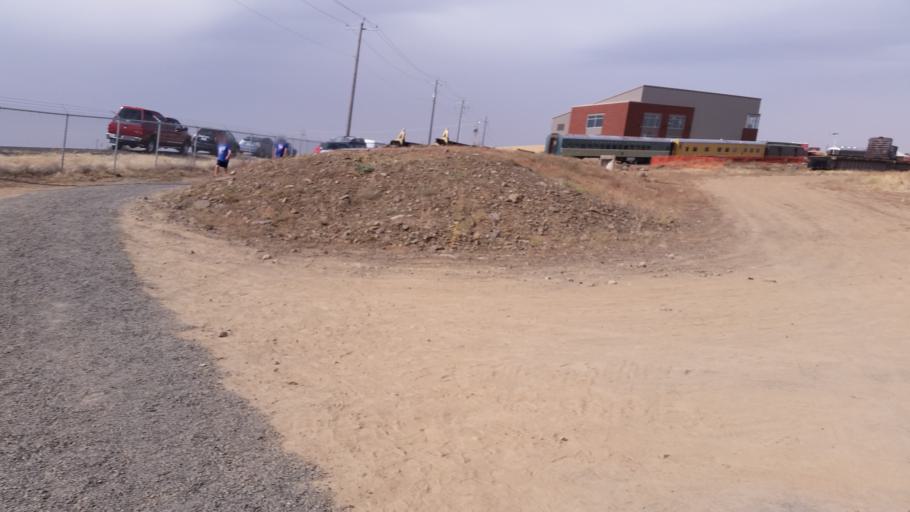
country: US
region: Washington
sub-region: Lincoln County
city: Davenport
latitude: 47.6624
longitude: -117.9377
